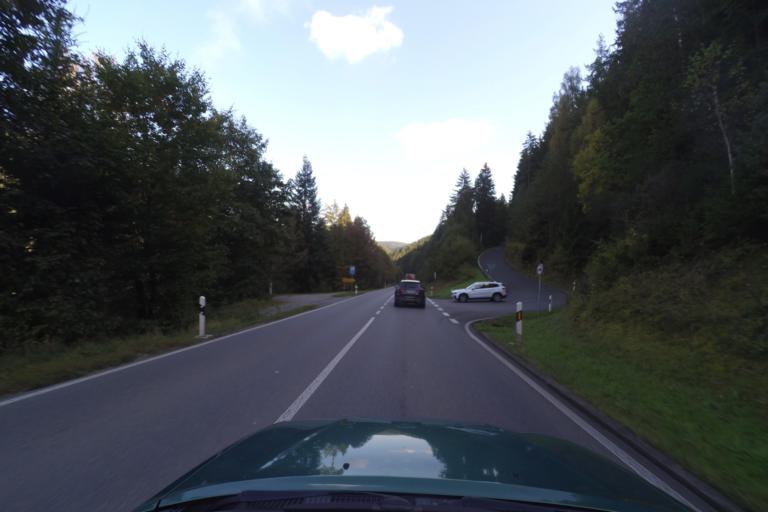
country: DE
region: Baden-Wuerttemberg
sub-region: Karlsruhe Region
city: Neubulach
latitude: 48.6770
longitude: 8.7122
